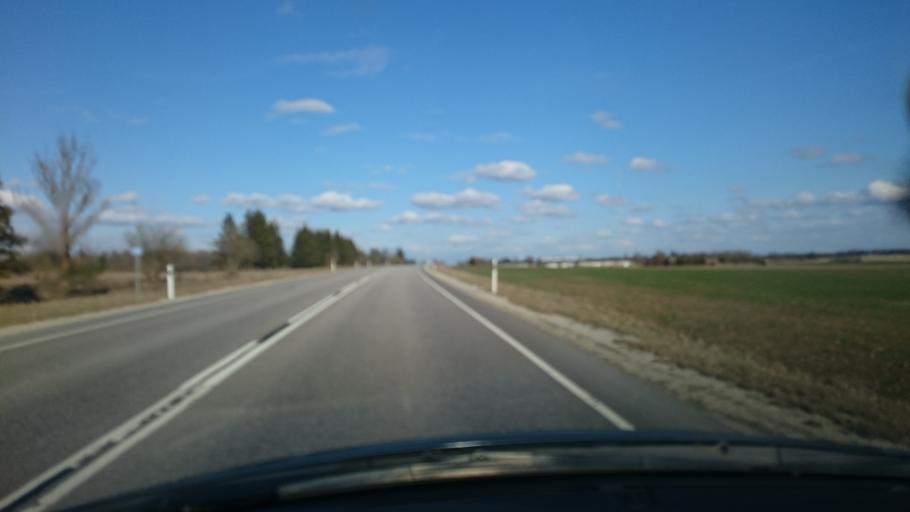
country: EE
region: Laeaene
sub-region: Lihula vald
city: Lihula
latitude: 58.7260
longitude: 23.9307
